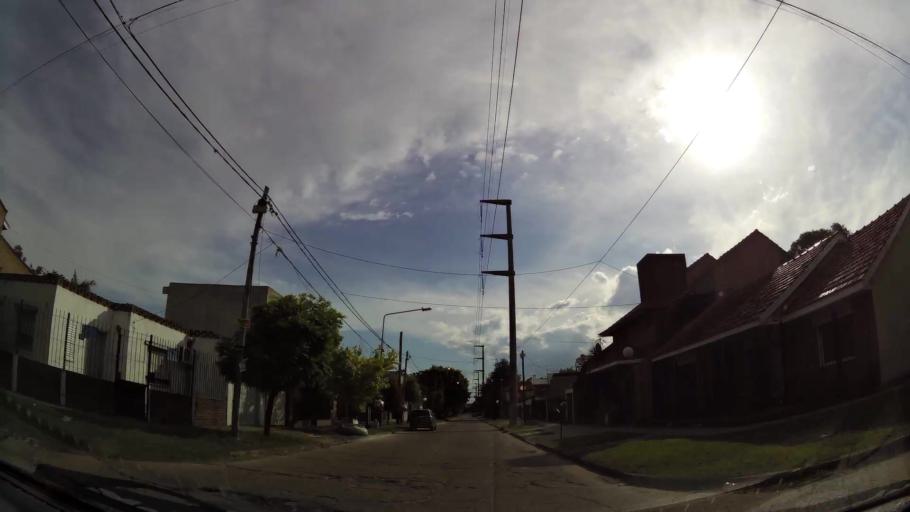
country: AR
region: Buenos Aires
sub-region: Partido de Quilmes
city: Quilmes
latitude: -34.7596
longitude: -58.2744
